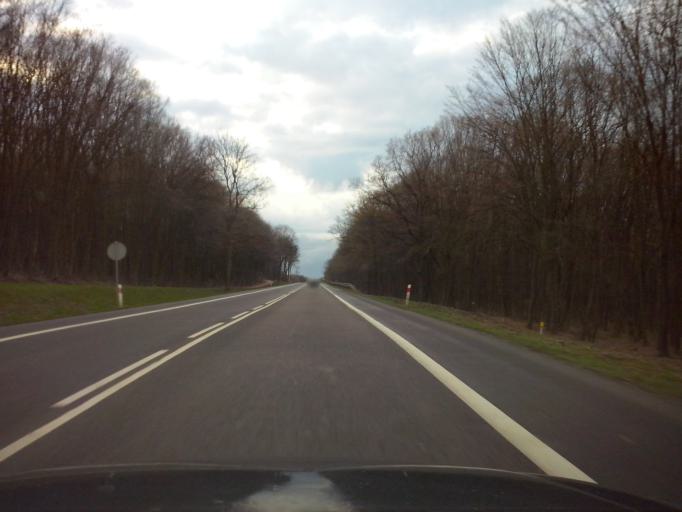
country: PL
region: Lublin Voivodeship
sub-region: Chelm
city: Chelm
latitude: 51.1528
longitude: 23.4171
